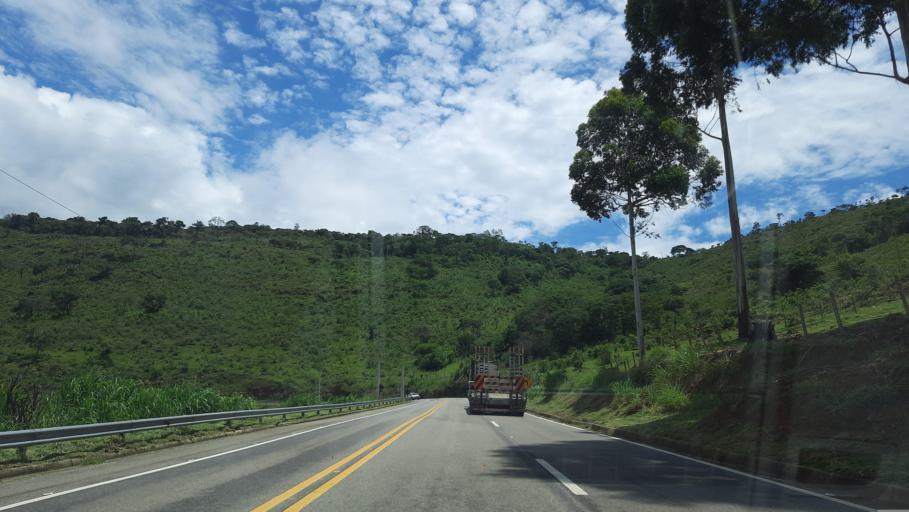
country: BR
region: Sao Paulo
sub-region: Vargem Grande Do Sul
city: Vargem Grande do Sul
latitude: -21.8305
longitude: -46.7659
